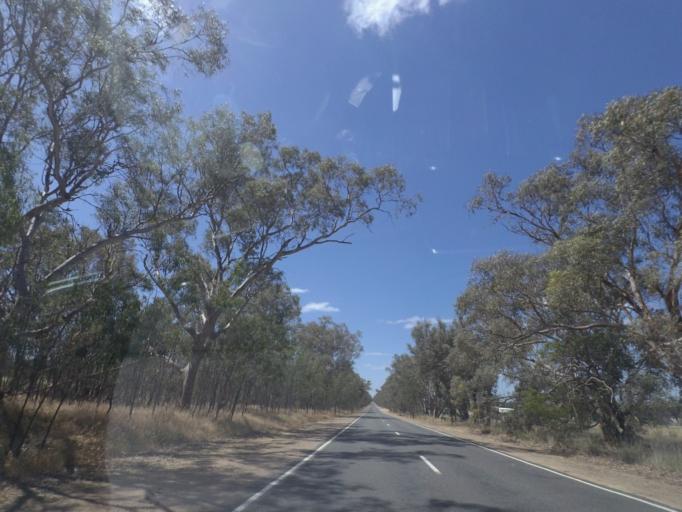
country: AU
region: Victoria
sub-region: Wangaratta
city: Wangaratta
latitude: -36.4405
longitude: 146.2460
